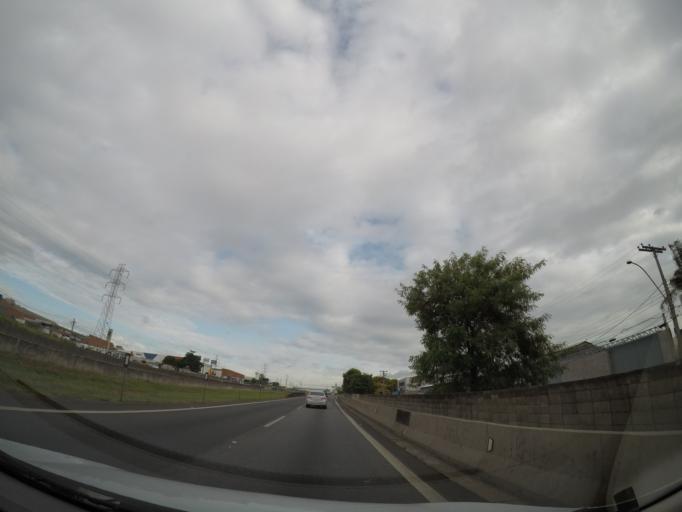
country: BR
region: Sao Paulo
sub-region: Campinas
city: Campinas
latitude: -22.9262
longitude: -47.0851
